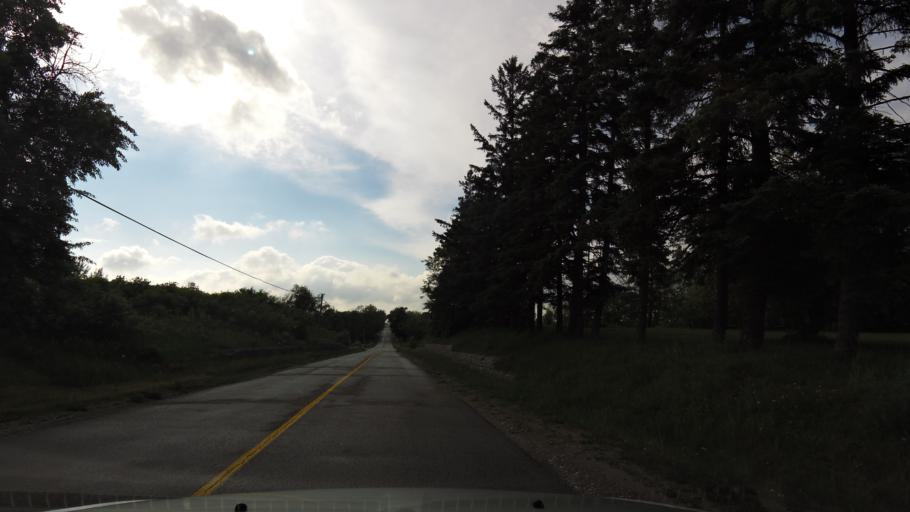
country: CA
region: Ontario
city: Ancaster
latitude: 43.0139
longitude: -80.0254
